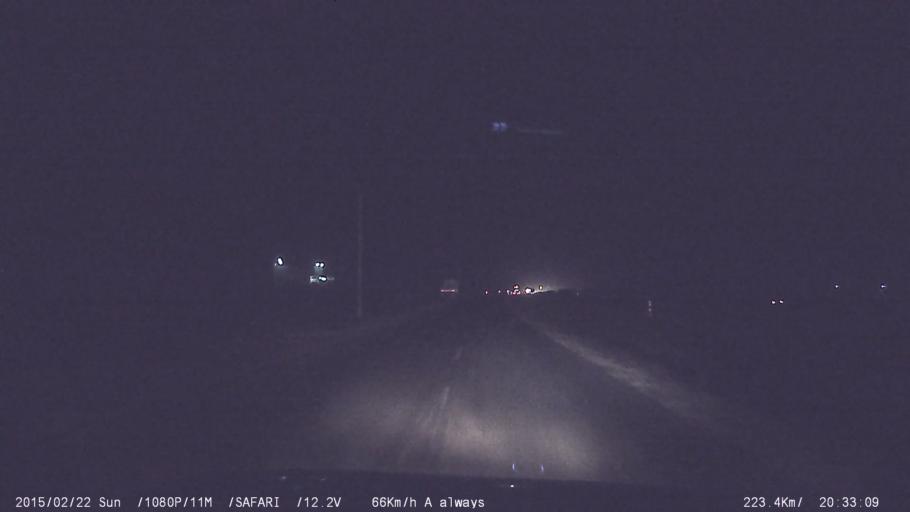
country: IN
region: Tamil Nadu
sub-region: Dindigul
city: Dindigul
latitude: 10.3546
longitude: 77.9494
